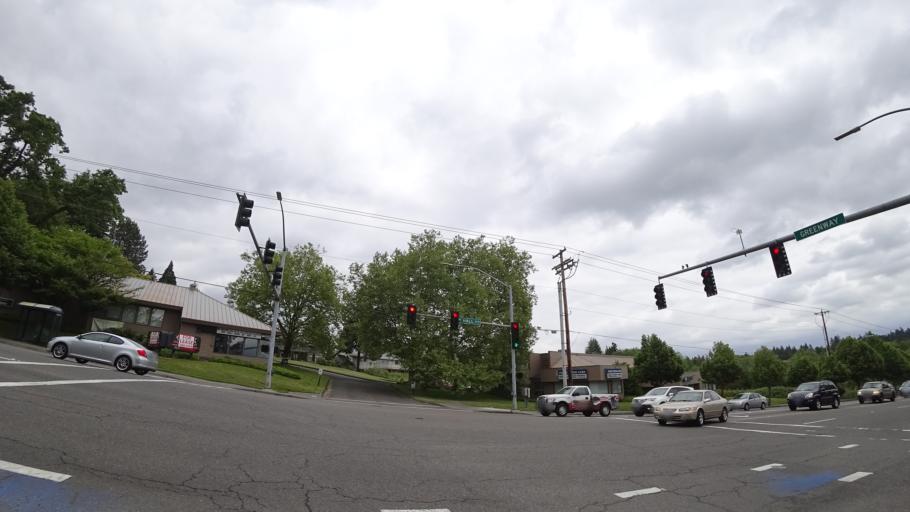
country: US
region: Oregon
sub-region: Washington County
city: Beaverton
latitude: 45.4614
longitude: -122.7970
